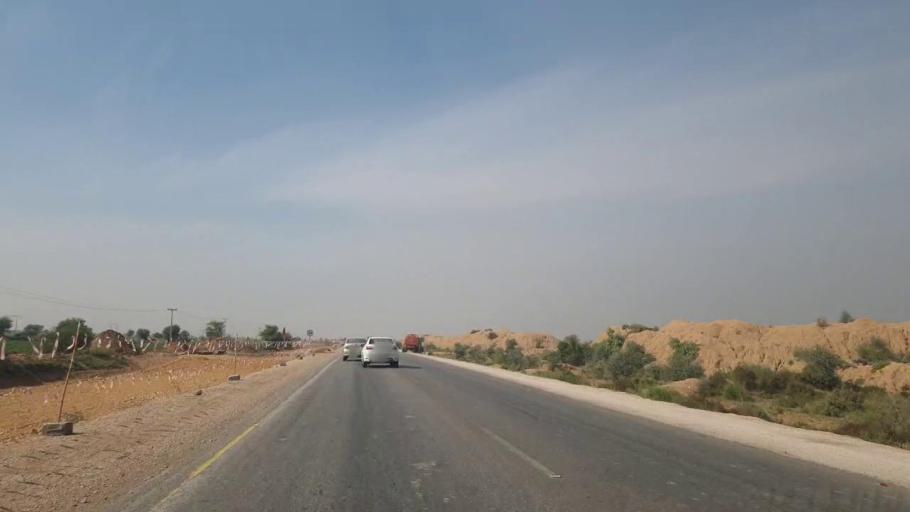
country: PK
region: Sindh
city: Sann
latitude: 26.0117
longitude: 68.1474
